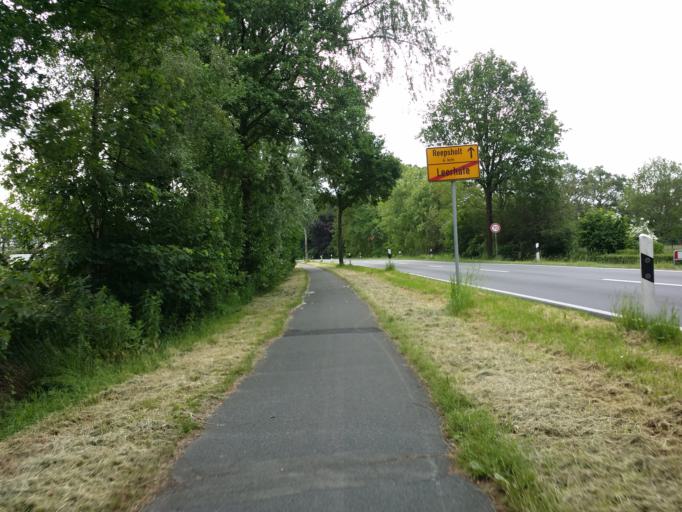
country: DE
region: Lower Saxony
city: Wittmund
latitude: 53.5253
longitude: 7.7819
